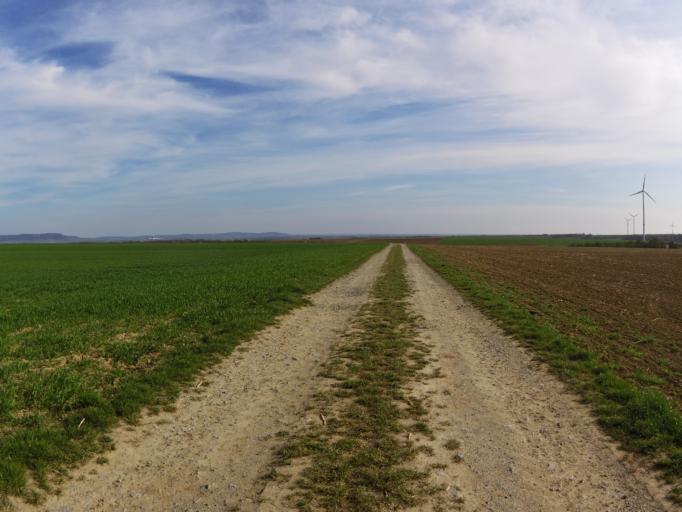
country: DE
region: Bavaria
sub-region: Regierungsbezirk Unterfranken
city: Mainstockheim
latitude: 49.7927
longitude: 10.1296
